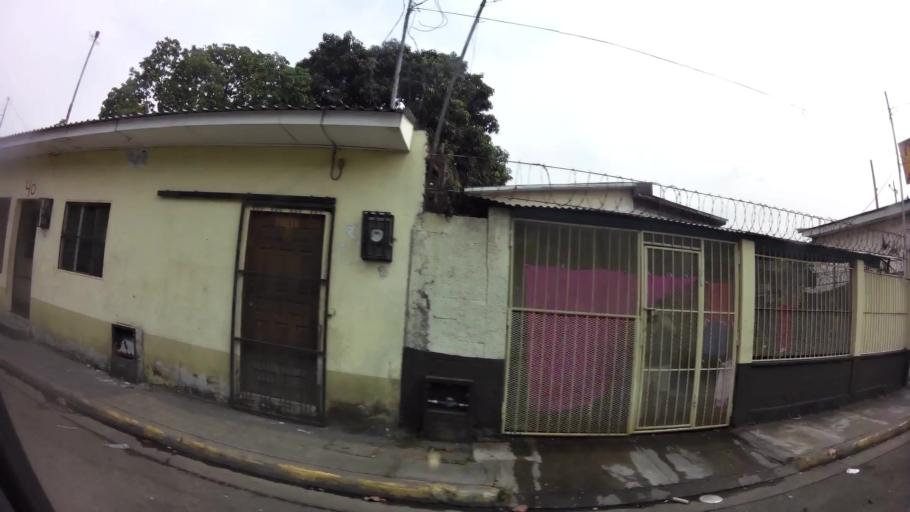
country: HN
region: Cortes
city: San Pedro Sula
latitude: 15.4939
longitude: -88.0215
